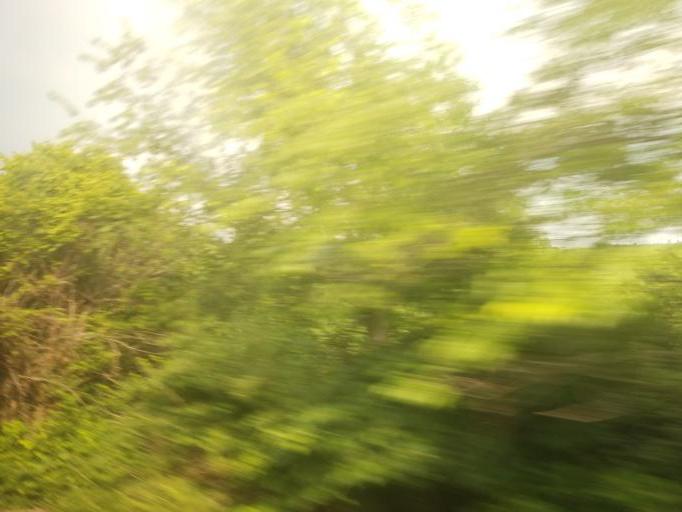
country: US
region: Illinois
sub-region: Bureau County
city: Princeton
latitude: 41.3399
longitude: -89.6508
